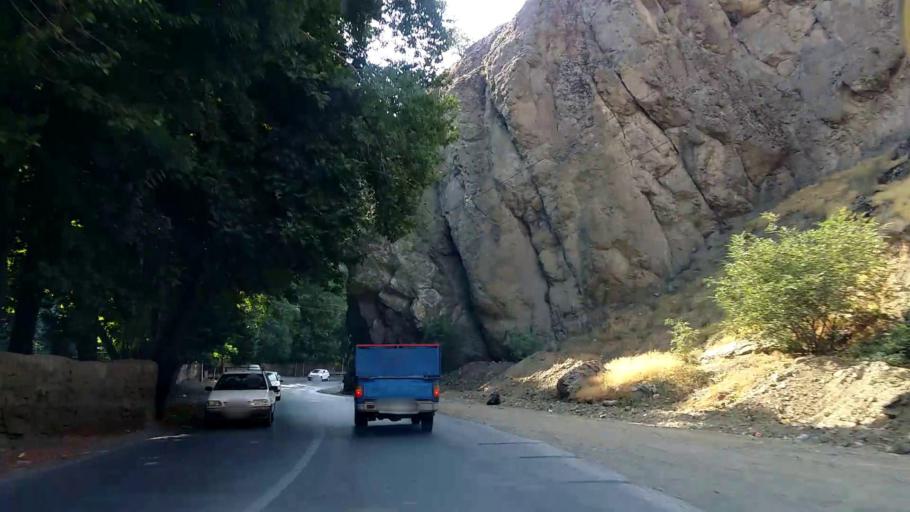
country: IR
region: Alborz
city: Karaj
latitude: 35.8786
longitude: 51.0424
